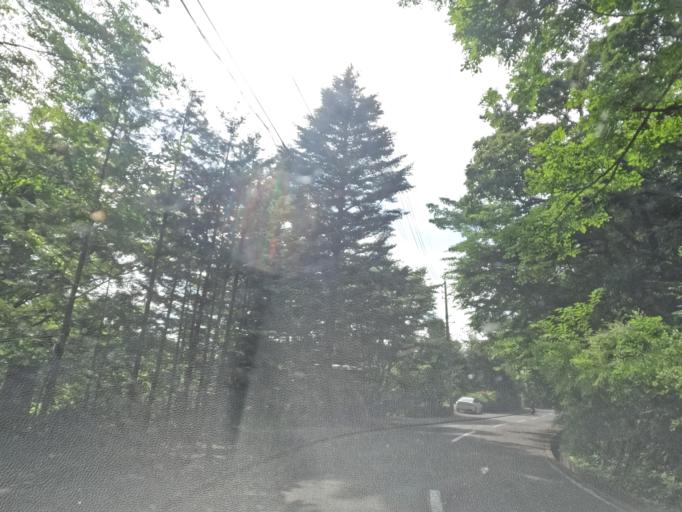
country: JP
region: Nagano
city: Komoro
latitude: 36.3547
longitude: 138.5926
